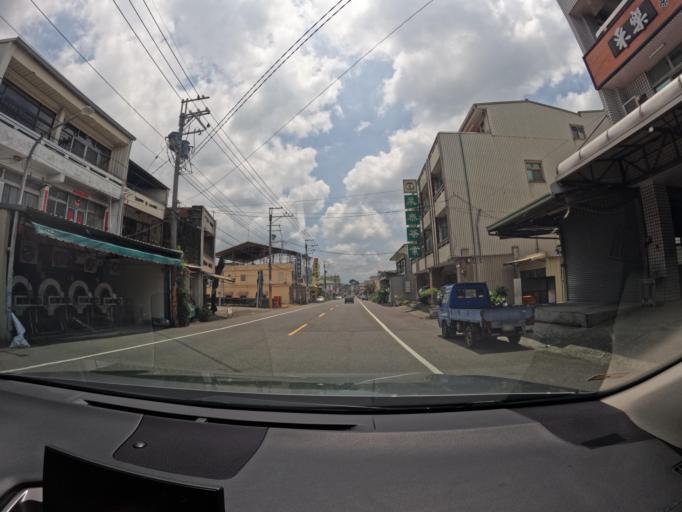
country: TW
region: Taiwan
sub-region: Nantou
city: Nantou
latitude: 23.8386
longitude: 120.6334
